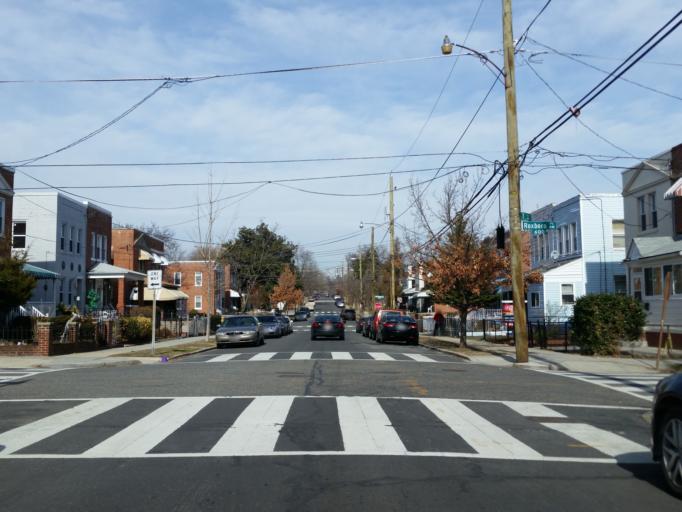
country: US
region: Maryland
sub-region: Montgomery County
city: Takoma Park
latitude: 38.9655
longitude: -77.0225
